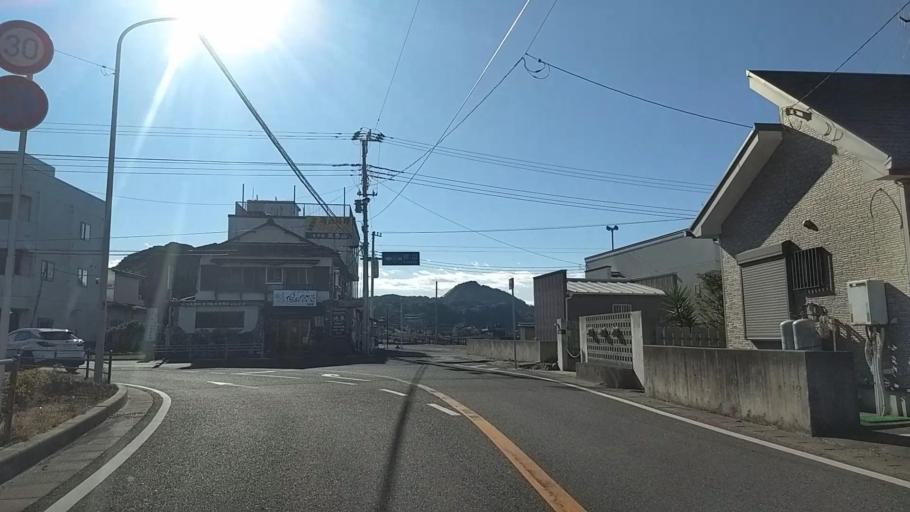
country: JP
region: Chiba
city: Tateyama
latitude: 35.1386
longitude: 139.8372
